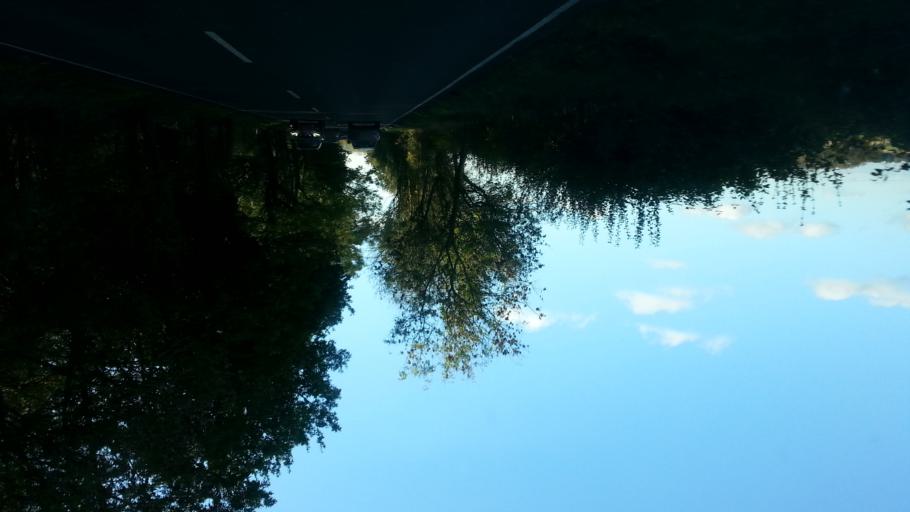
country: GB
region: England
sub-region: Suffolk
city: Beccles
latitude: 52.4800
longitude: 1.5319
